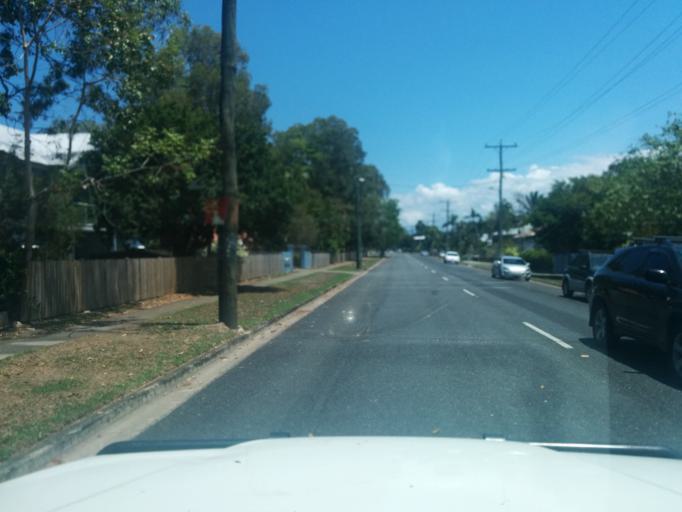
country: AU
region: Queensland
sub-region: Cairns
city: Cairns
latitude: -16.9075
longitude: 145.7552
